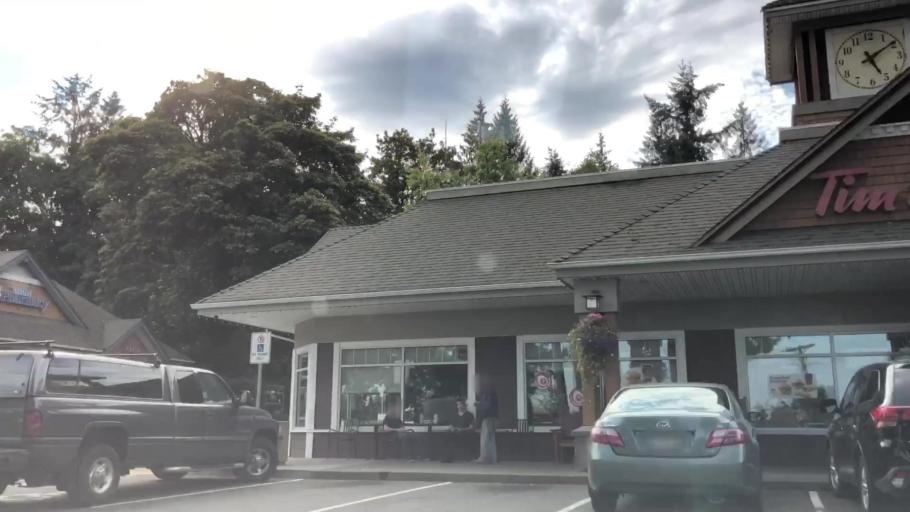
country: CA
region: British Columbia
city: North Saanich
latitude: 48.6521
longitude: -123.5611
